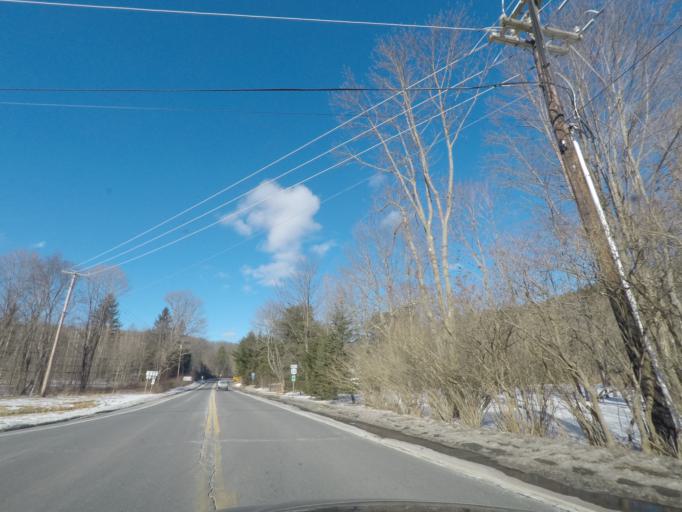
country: US
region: Massachusetts
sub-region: Berkshire County
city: West Stockbridge
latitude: 42.3125
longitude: -73.4732
